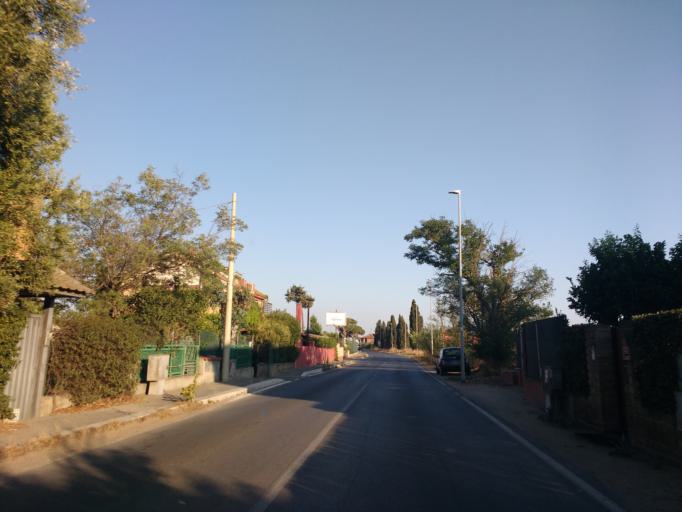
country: IT
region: Latium
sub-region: Citta metropolitana di Roma Capitale
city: Focene
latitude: 41.8360
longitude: 12.2297
